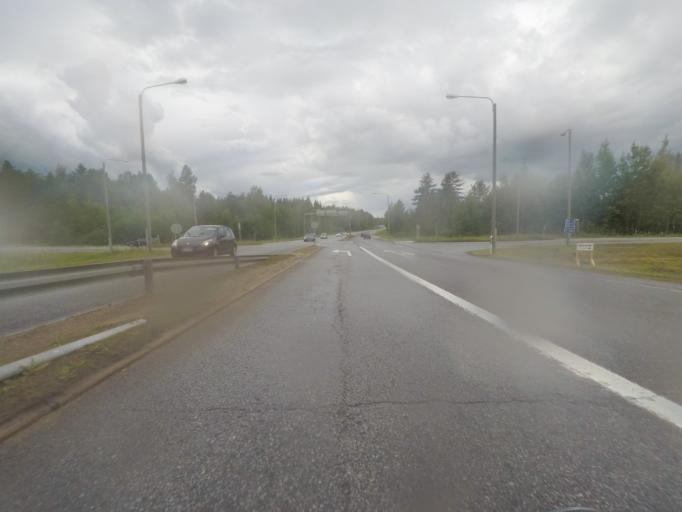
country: FI
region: Central Finland
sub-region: Jyvaeskylae
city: Toivakka
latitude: 62.2501
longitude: 26.1767
